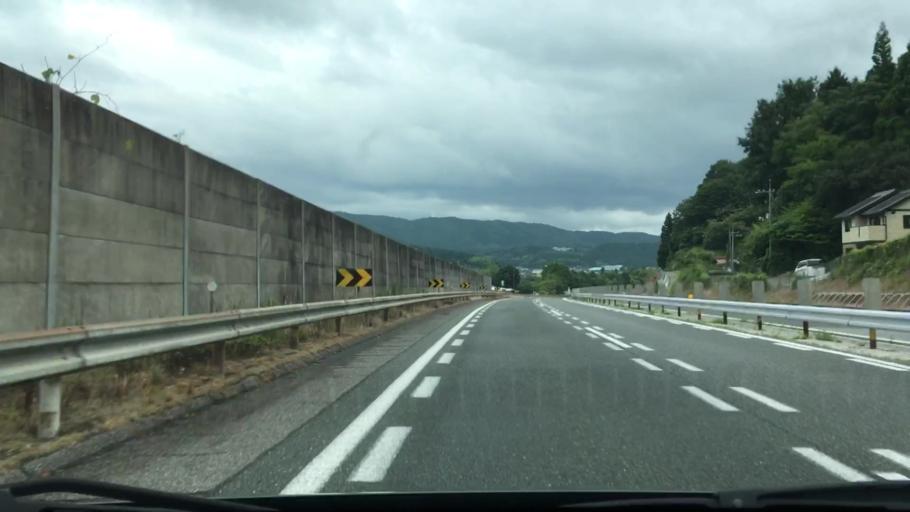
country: JP
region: Okayama
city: Niimi
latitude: 34.9502
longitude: 133.3296
